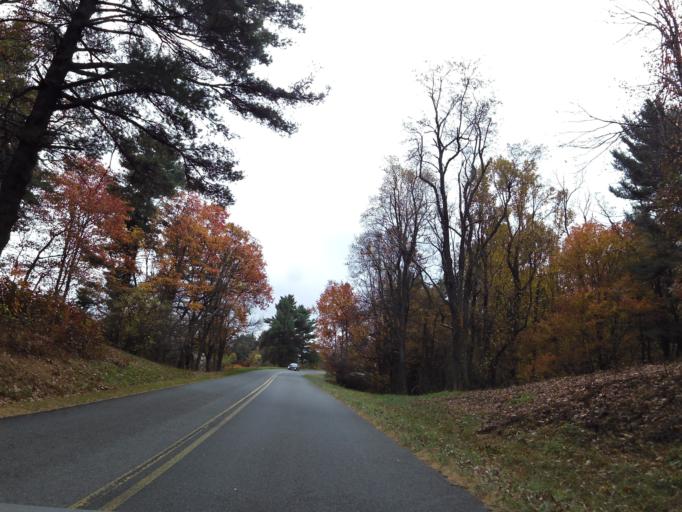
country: US
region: Virginia
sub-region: Carroll County
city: Cana
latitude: 36.6516
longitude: -80.7107
